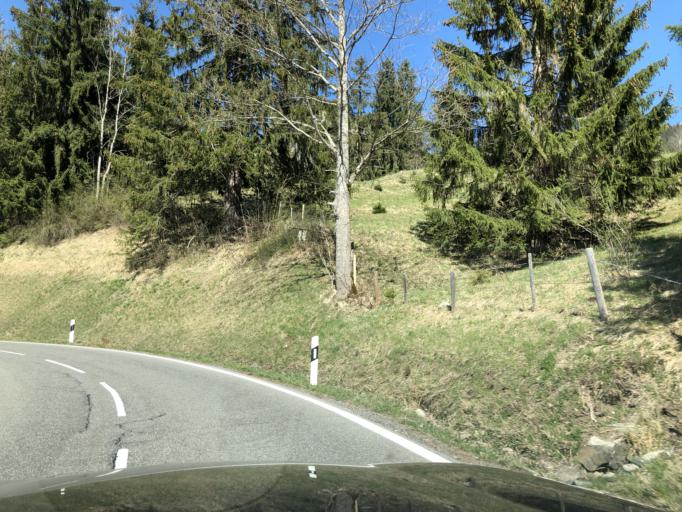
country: AT
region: Tyrol
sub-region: Politischer Bezirk Reutte
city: Schattwald
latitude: 47.5081
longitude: 10.3872
